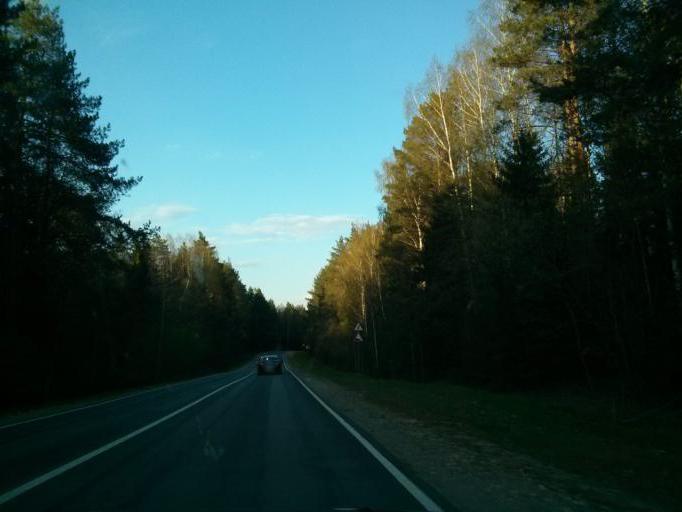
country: RU
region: Nizjnij Novgorod
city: Savasleyka
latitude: 55.7475
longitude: 42.4538
